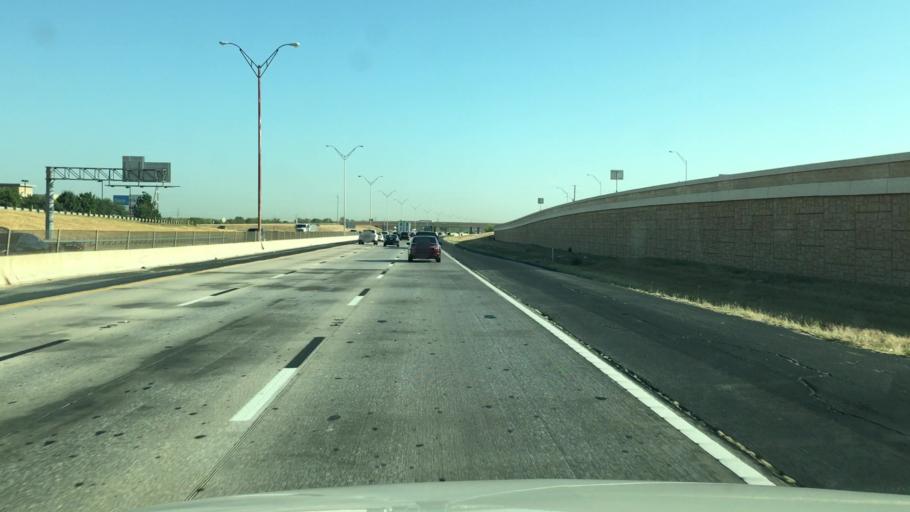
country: US
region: Texas
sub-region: Johnson County
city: Burleson
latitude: 32.5726
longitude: -97.3190
